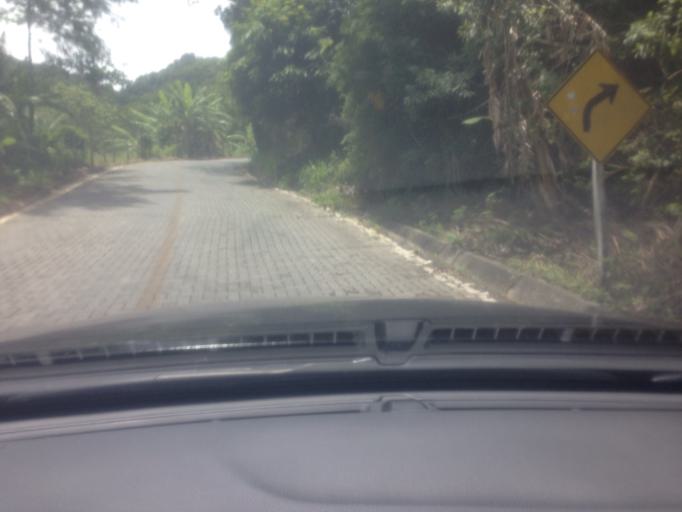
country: BR
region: Espirito Santo
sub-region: Guarapari
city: Guarapari
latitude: -20.6071
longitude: -40.5363
